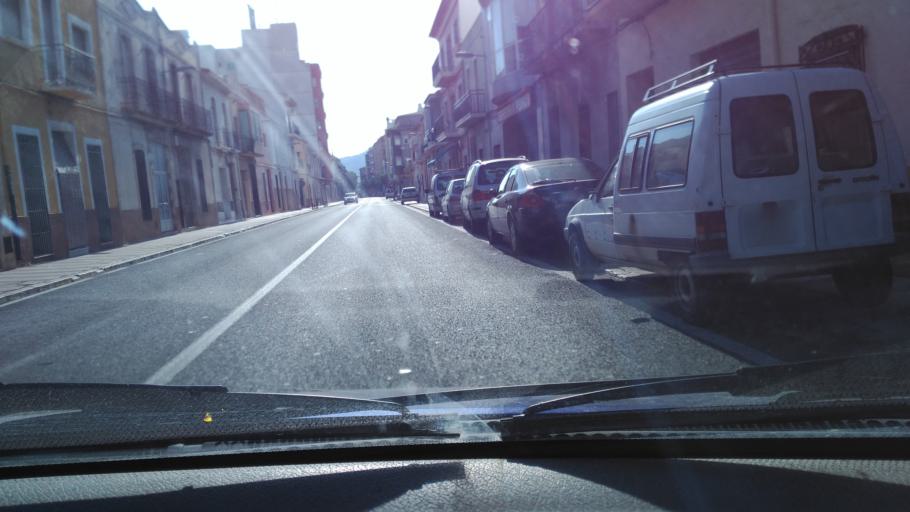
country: ES
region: Valencia
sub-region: Provincia de Alicante
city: Gata de Gorgos
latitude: 38.7733
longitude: 0.0881
